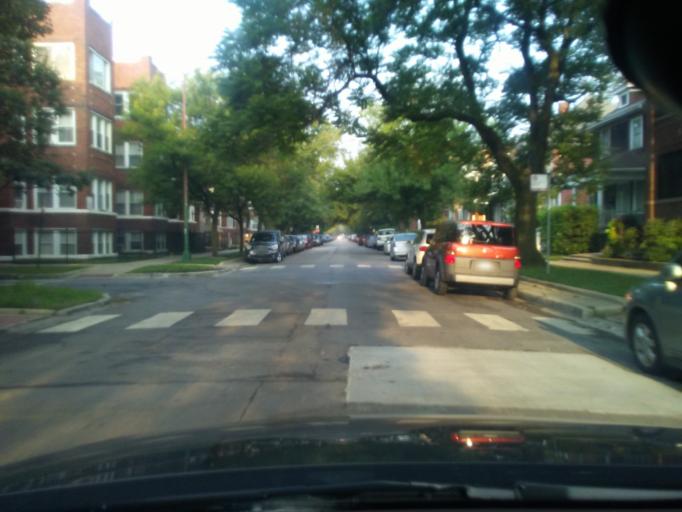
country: US
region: Illinois
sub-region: Cook County
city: Lincolnwood
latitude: 41.9647
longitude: -87.7045
